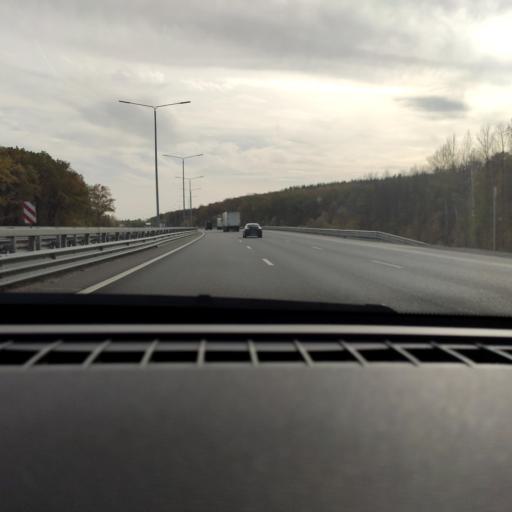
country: RU
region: Voronezj
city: Podgornoye
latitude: 51.8028
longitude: 39.2540
